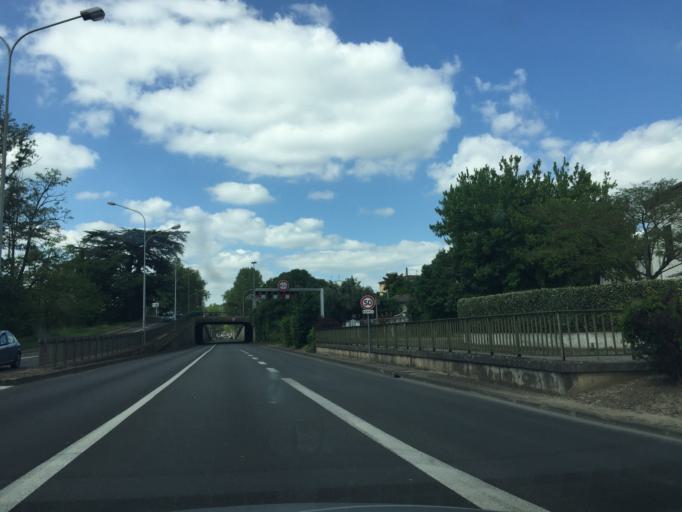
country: FR
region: Aquitaine
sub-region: Departement du Lot-et-Garonne
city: Le Passage
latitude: 44.1936
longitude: 0.6125
